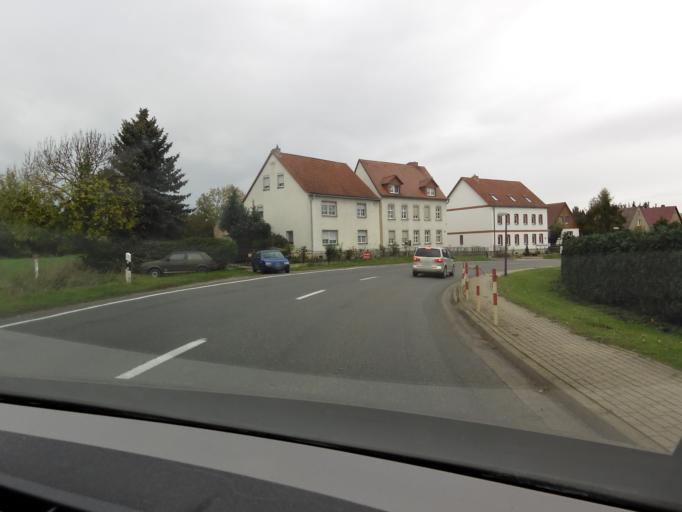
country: DE
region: Saxony-Anhalt
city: Zeitz
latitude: 51.0951
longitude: 12.1757
